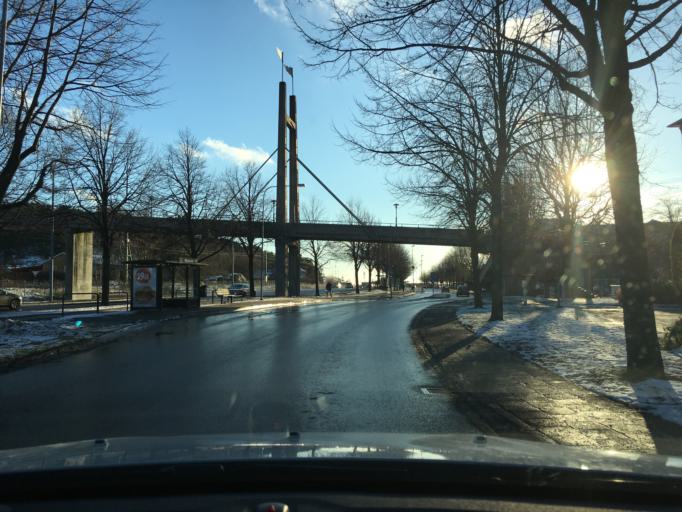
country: SE
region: Vaestra Goetaland
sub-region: Stenungsunds Kommun
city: Stenungsund
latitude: 58.0668
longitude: 11.8188
